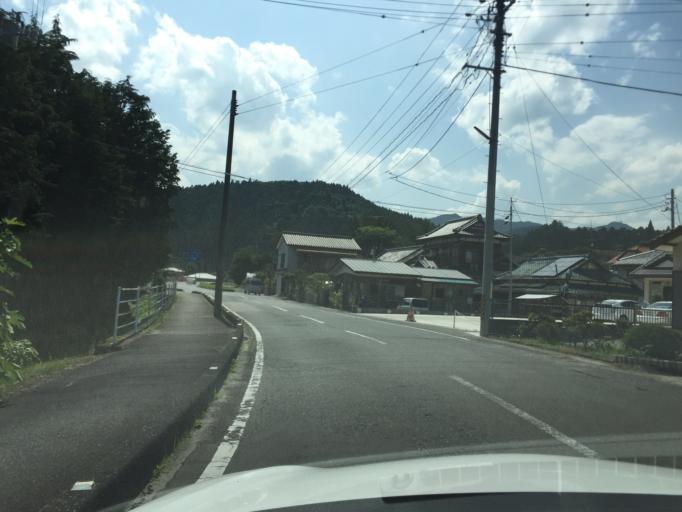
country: JP
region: Ibaraki
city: Kitaibaraki
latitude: 36.9219
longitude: 140.7422
